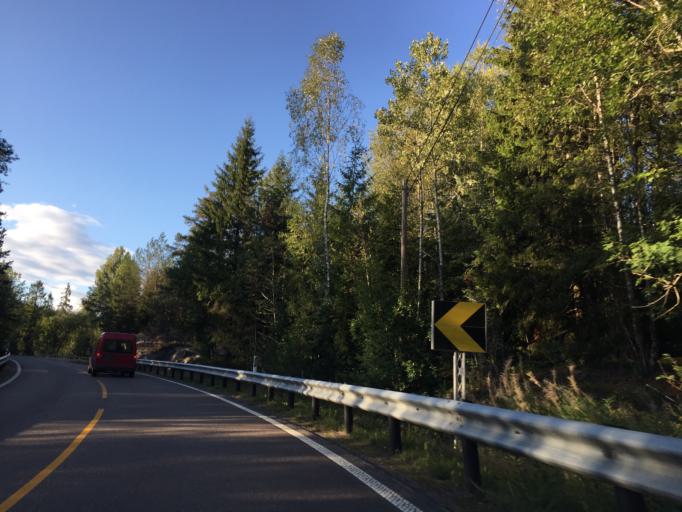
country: NO
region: Akershus
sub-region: Enebakk
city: Flateby
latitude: 59.8271
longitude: 11.2429
